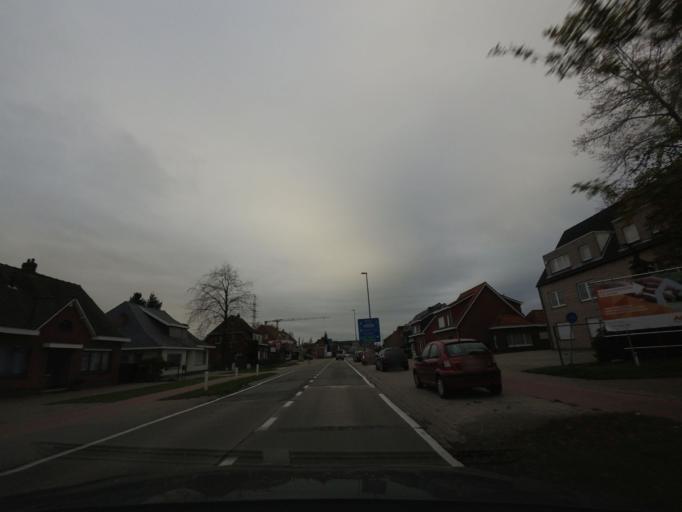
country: BE
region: Flanders
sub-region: Provincie Antwerpen
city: Schilde
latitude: 51.3055
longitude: 4.5703
